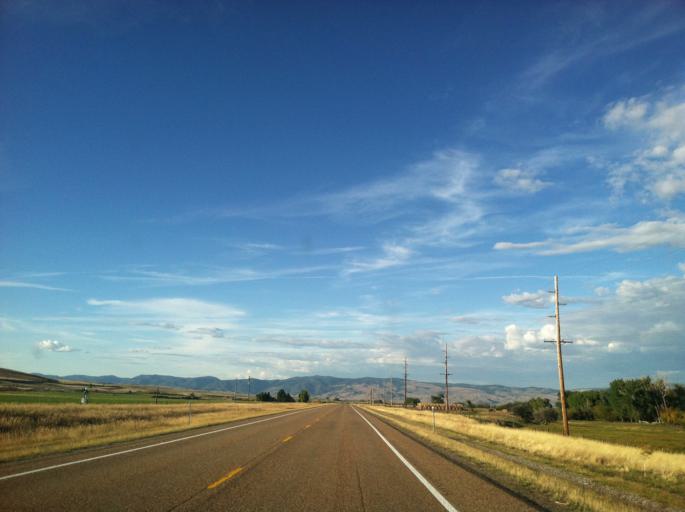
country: US
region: Montana
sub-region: Granite County
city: Philipsburg
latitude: 46.5470
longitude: -113.2190
